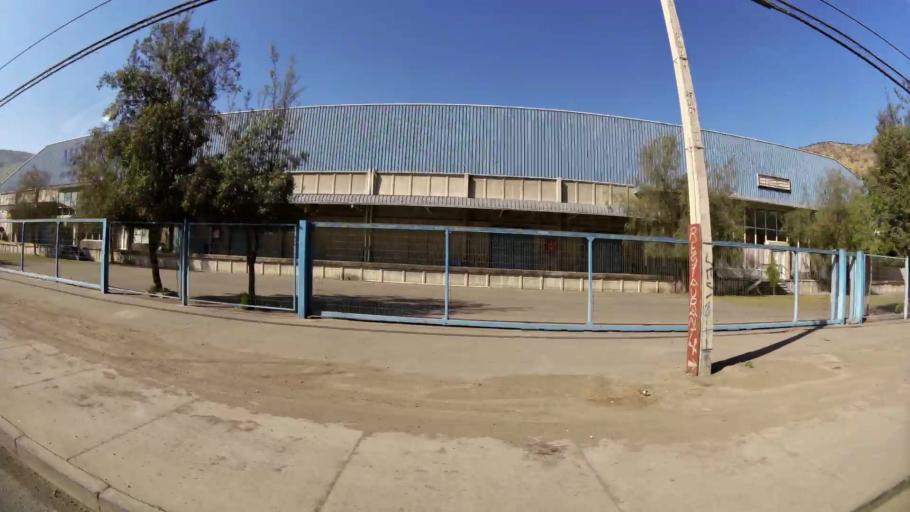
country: CL
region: Santiago Metropolitan
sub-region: Provincia de Chacabuco
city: Chicureo Abajo
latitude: -33.3390
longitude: -70.6948
